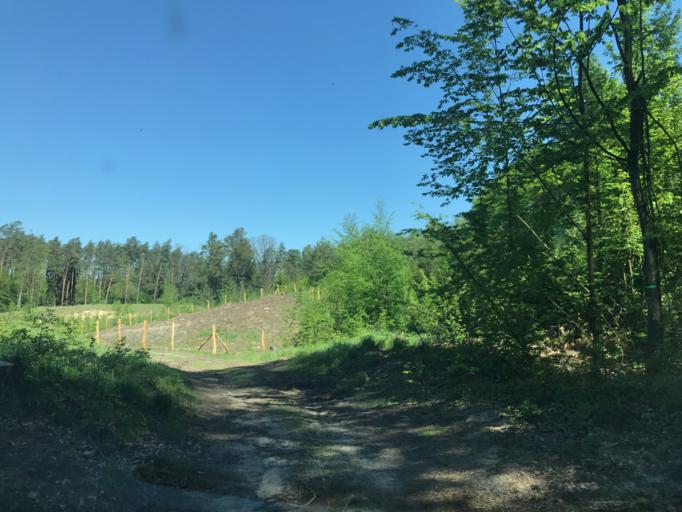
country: PL
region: Kujawsko-Pomorskie
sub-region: Powiat brodnicki
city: Gorzno
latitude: 53.2119
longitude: 19.6938
